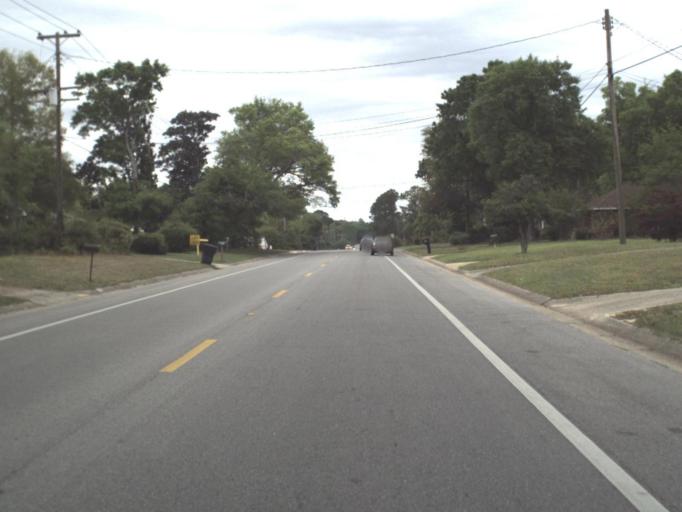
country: US
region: Florida
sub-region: Escambia County
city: Goulding
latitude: 30.4600
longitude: -87.2001
